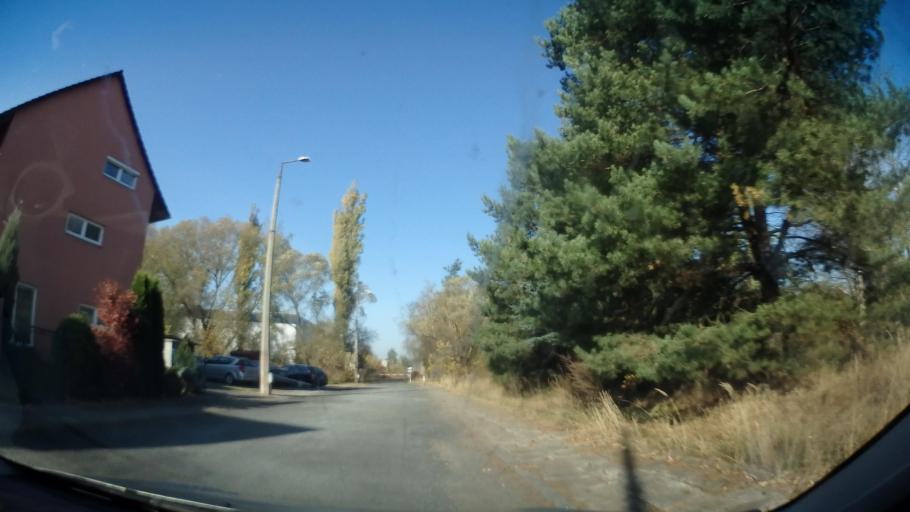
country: CZ
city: Tyniste nad Orlici
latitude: 50.1593
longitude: 16.0673
